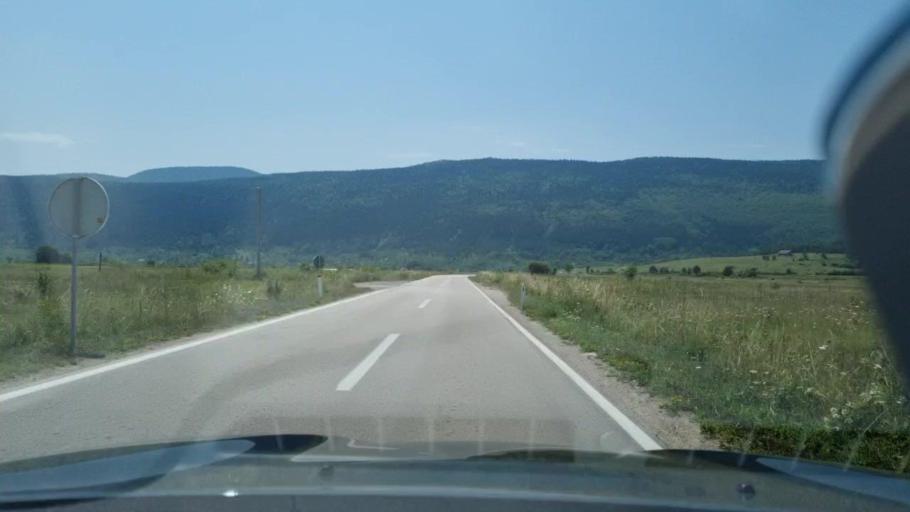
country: BA
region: Federation of Bosnia and Herzegovina
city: Orasac
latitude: 44.5314
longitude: 16.3523
